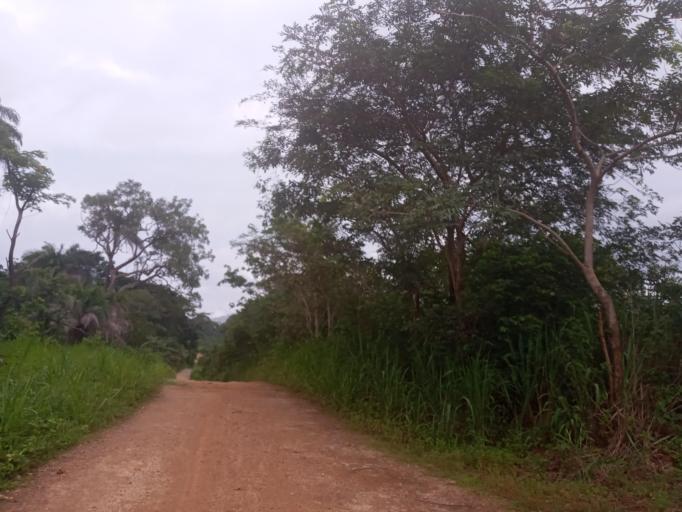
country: SL
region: Northern Province
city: Bumbuna
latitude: 8.9619
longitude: -11.7579
